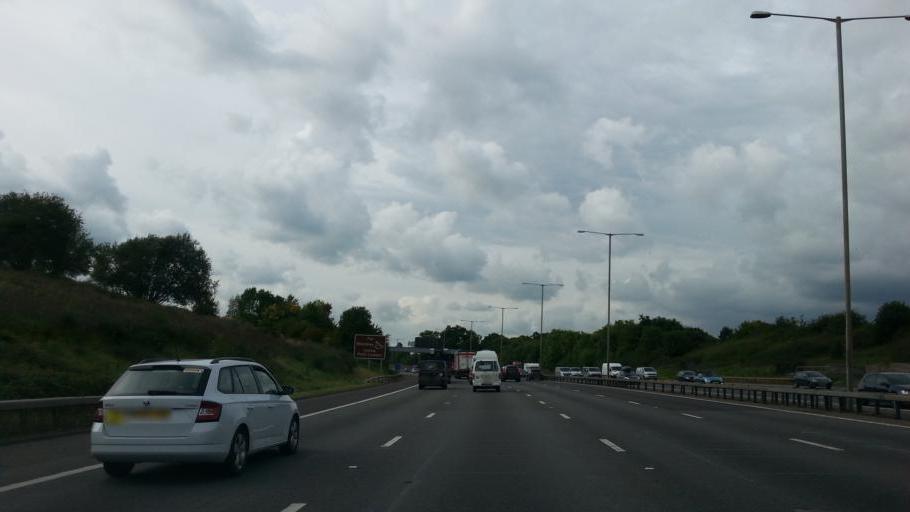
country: GB
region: England
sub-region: Buckinghamshire
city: Denham
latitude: 51.5441
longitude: -0.5061
